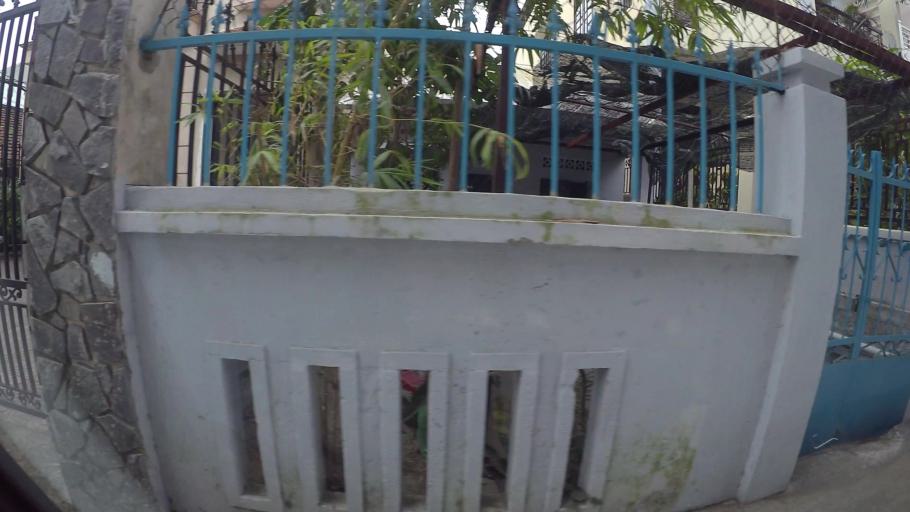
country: VN
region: Da Nang
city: Son Tra
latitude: 16.0490
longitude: 108.2396
